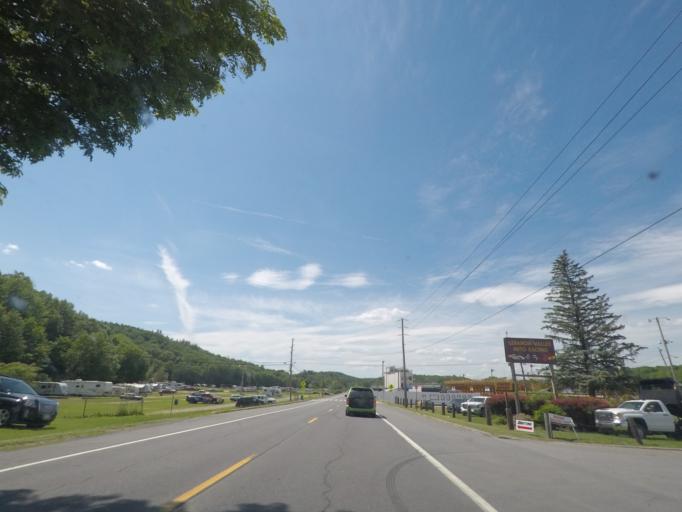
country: US
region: New York
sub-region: Rensselaer County
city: Nassau
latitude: 42.4899
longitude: -73.4869
